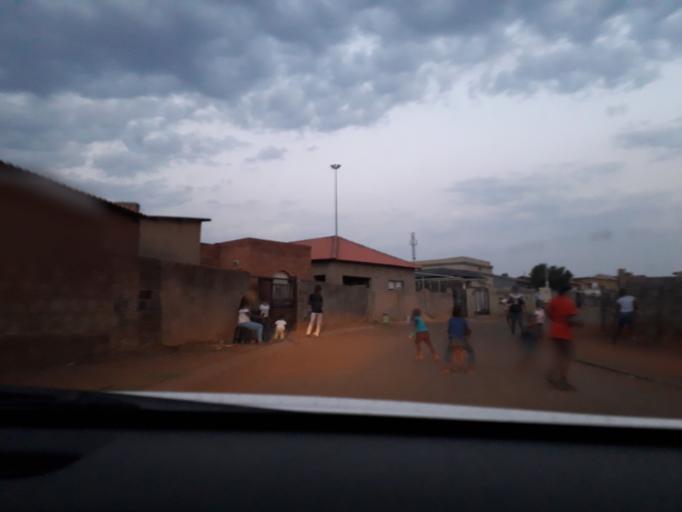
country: ZA
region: Gauteng
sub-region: Ekurhuleni Metropolitan Municipality
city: Tembisa
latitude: -25.9993
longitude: 28.2386
